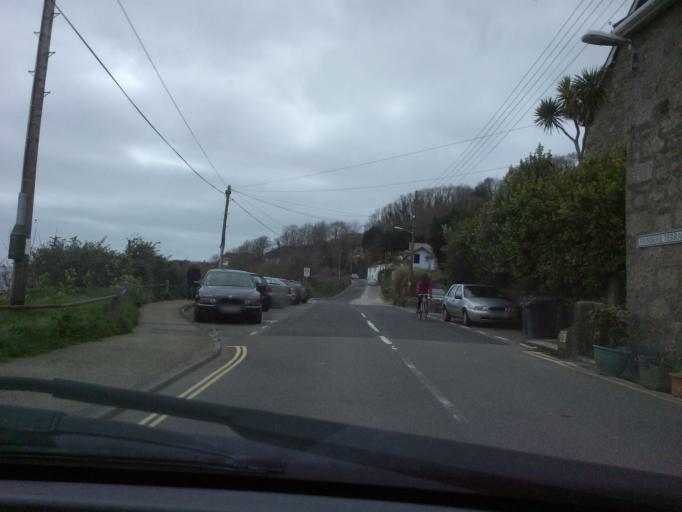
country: GB
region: England
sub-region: Cornwall
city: Penzance
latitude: 50.1005
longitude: -5.5445
